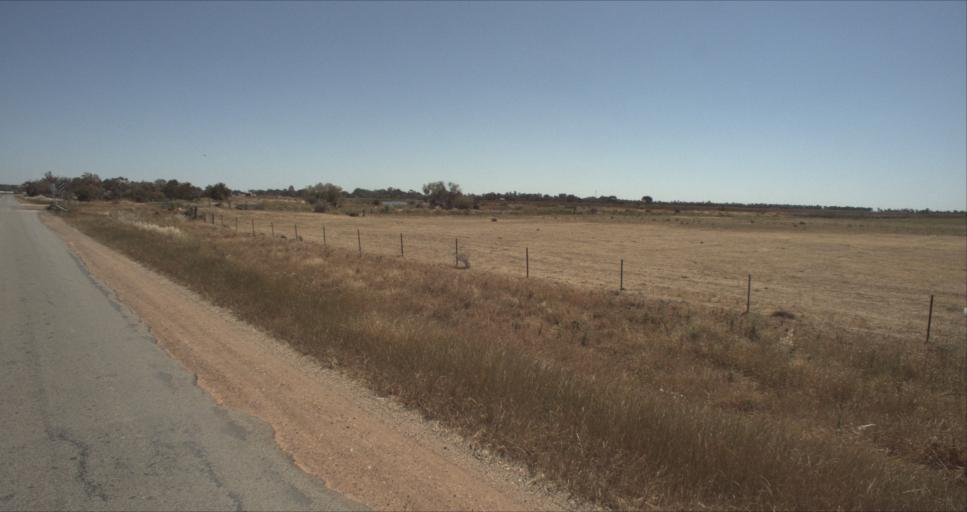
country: AU
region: New South Wales
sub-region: Leeton
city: Leeton
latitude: -34.5422
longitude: 146.4338
